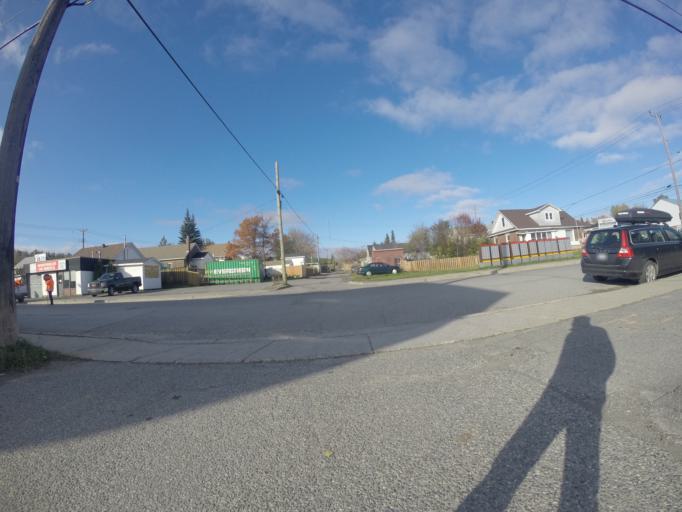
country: CA
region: Ontario
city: Greater Sudbury
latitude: 46.5022
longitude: -81.0064
